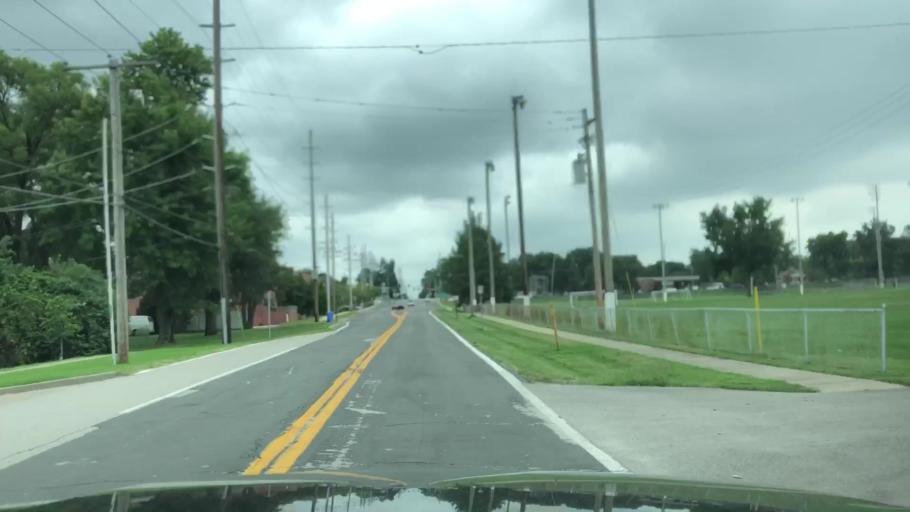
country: US
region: Missouri
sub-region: Saint Louis County
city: Hazelwood
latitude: 38.8106
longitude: -90.3617
